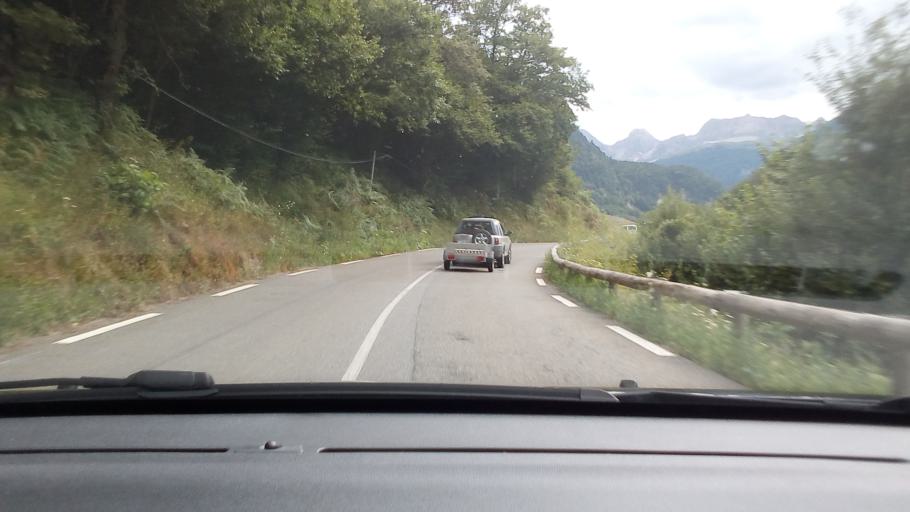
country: ES
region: Aragon
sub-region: Provincia de Huesca
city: Canfranc
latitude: 42.8581
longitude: -0.5487
